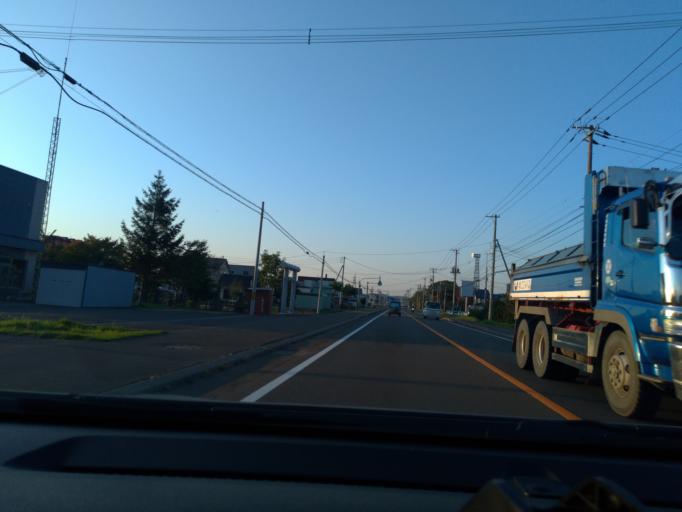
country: JP
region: Hokkaido
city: Tobetsu
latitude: 43.2066
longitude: 141.5198
